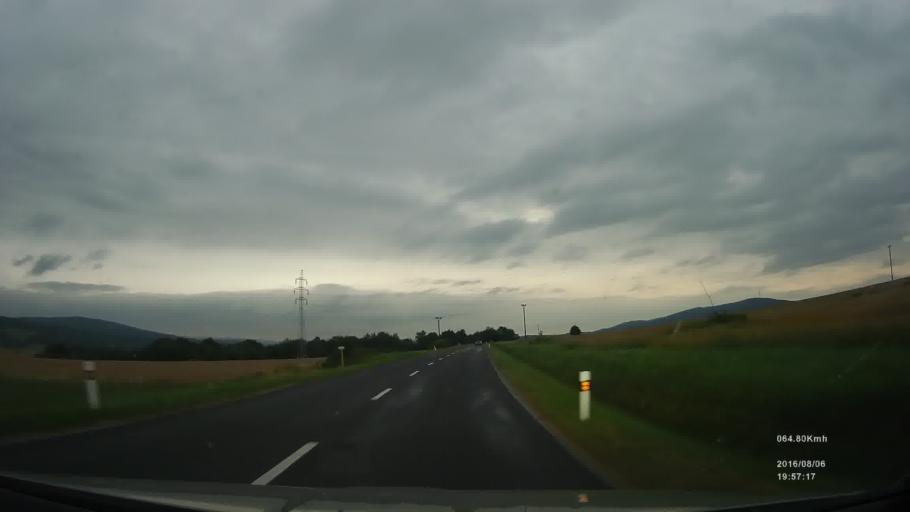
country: SK
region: Presovsky
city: Svidnik
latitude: 49.2775
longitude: 21.5739
